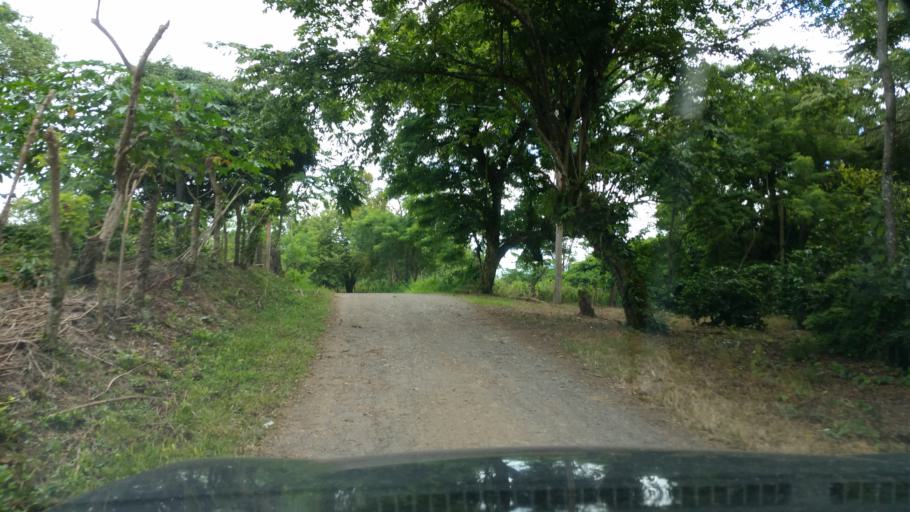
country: NI
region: Atlantico Norte (RAAN)
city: Waslala
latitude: 13.2659
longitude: -85.6205
